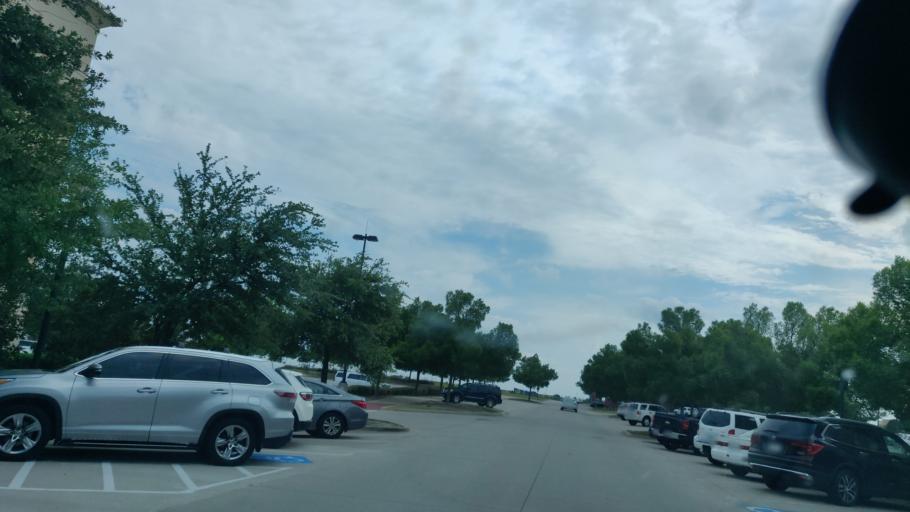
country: US
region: Texas
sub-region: Dallas County
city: Sachse
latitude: 32.9523
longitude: -96.6100
